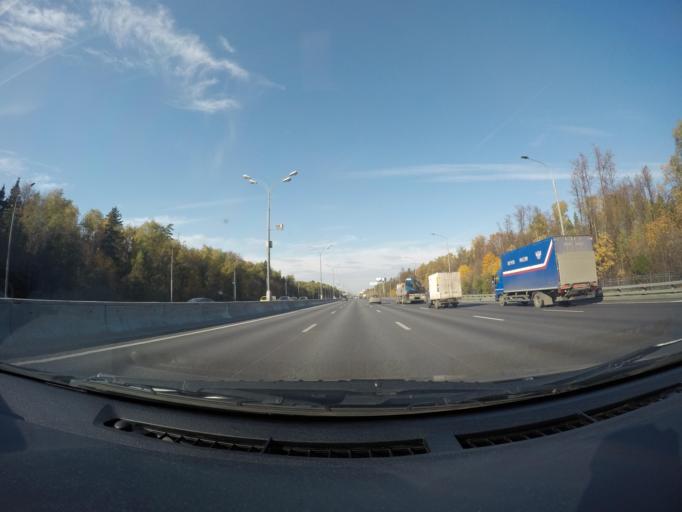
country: RU
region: Moscow
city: Gol'yanovo
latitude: 55.8422
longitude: 37.8044
